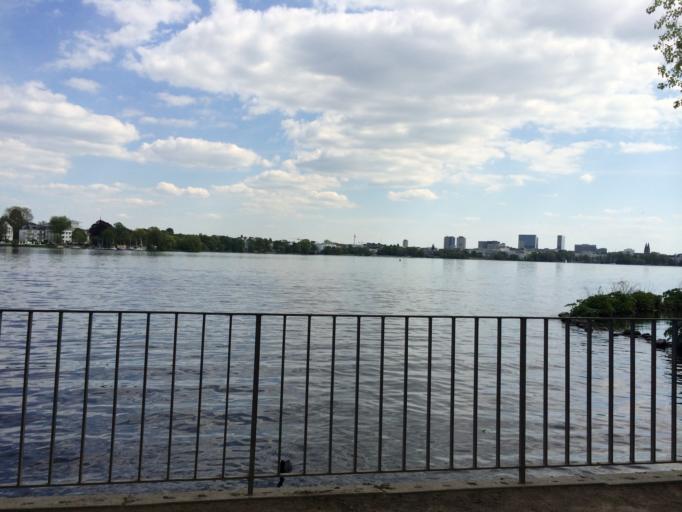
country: DE
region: Hamburg
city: Hamburg
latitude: 53.5713
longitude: 10.0024
